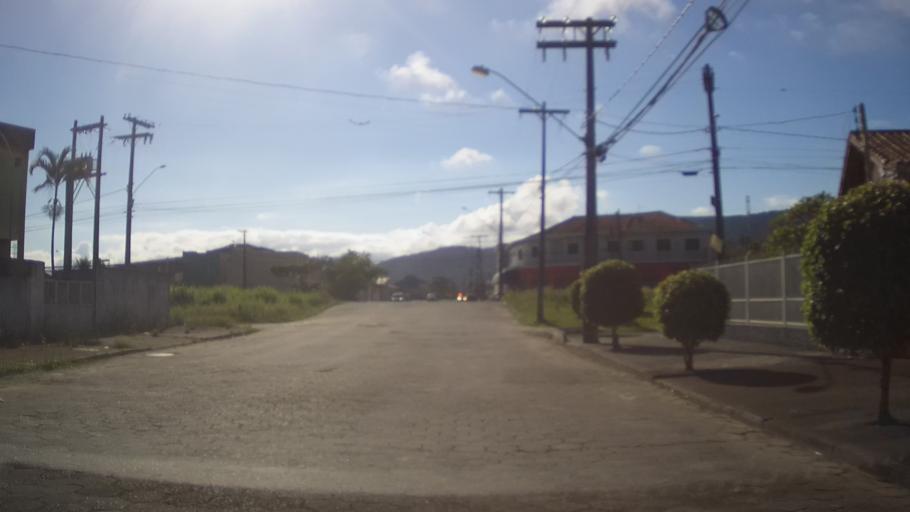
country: BR
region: Sao Paulo
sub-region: Itanhaem
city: Itanhaem
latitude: -24.1564
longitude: -46.7387
